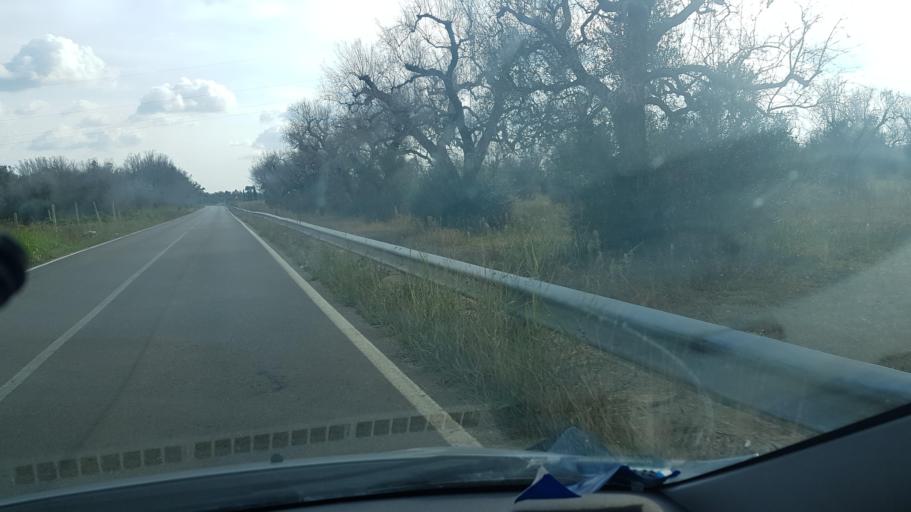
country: IT
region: Apulia
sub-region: Provincia di Brindisi
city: Cellino San Marco
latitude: 40.4484
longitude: 17.9546
